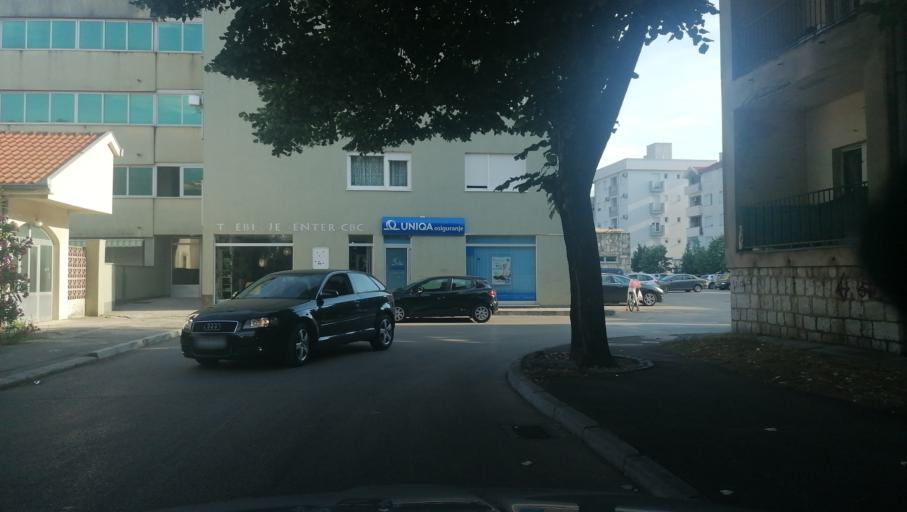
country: BA
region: Republika Srpska
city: Trebinje
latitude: 42.7070
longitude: 18.3471
